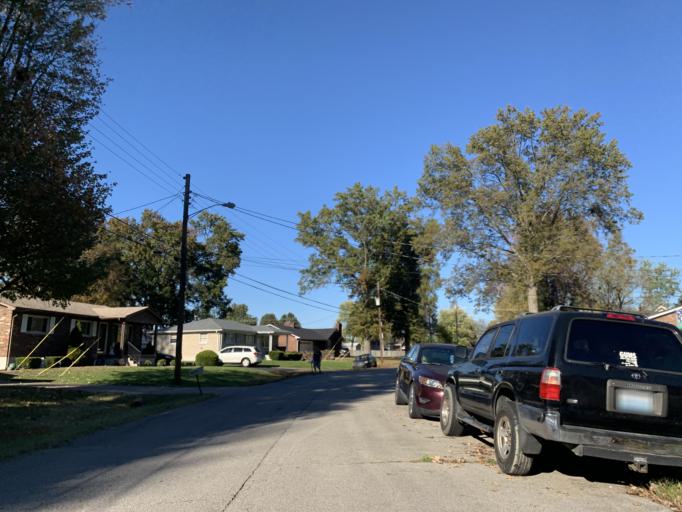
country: US
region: Kentucky
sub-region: Jefferson County
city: Pleasure Ridge Park
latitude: 38.1626
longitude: -85.8639
